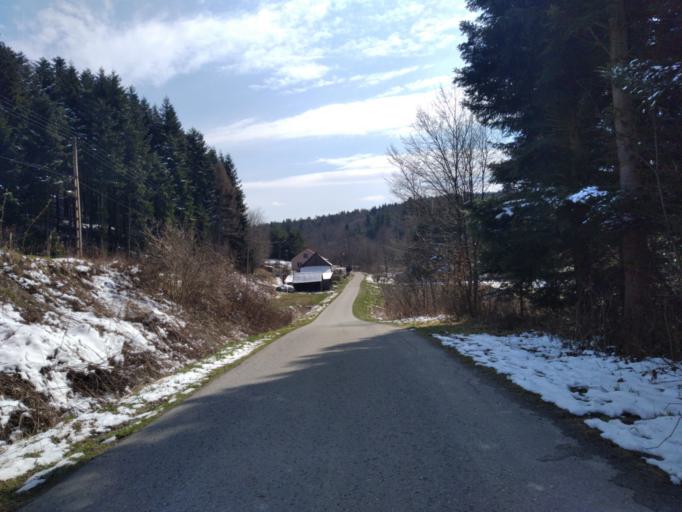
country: PL
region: Subcarpathian Voivodeship
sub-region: Powiat ropczycko-sedziszowski
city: Ropczyce
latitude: 50.0041
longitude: 21.5877
